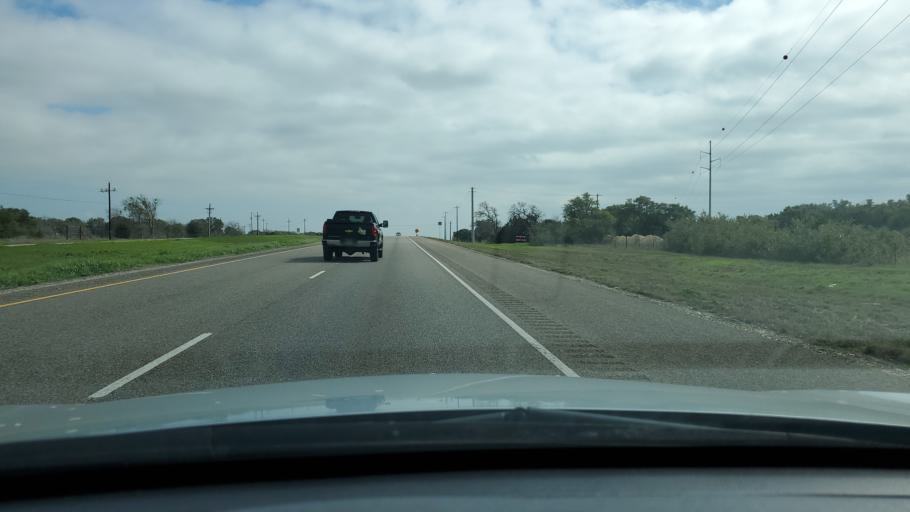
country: US
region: Texas
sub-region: Williamson County
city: Serenada
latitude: 30.7590
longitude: -97.7290
